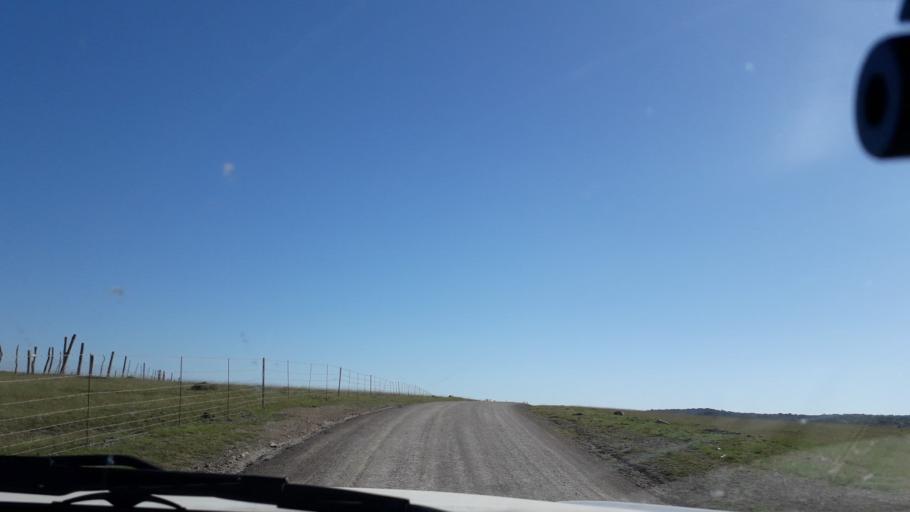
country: ZA
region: Eastern Cape
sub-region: Buffalo City Metropolitan Municipality
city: East London
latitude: -32.7978
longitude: 27.9534
